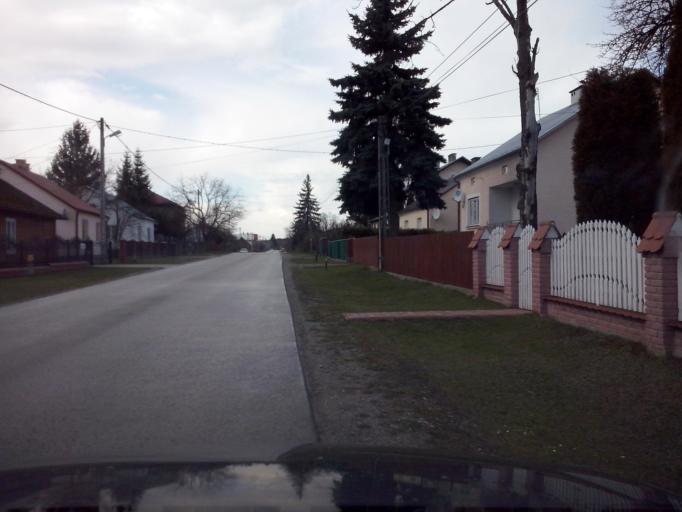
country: PL
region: Subcarpathian Voivodeship
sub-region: Powiat nizanski
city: Krzeszow
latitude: 50.4224
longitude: 22.3233
